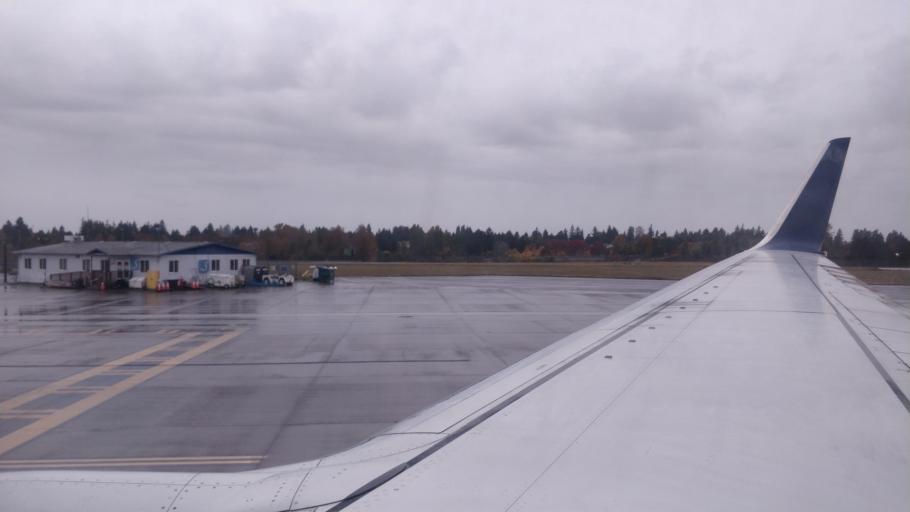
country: US
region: Washington
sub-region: King County
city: SeaTac
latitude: 47.4398
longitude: -122.3148
